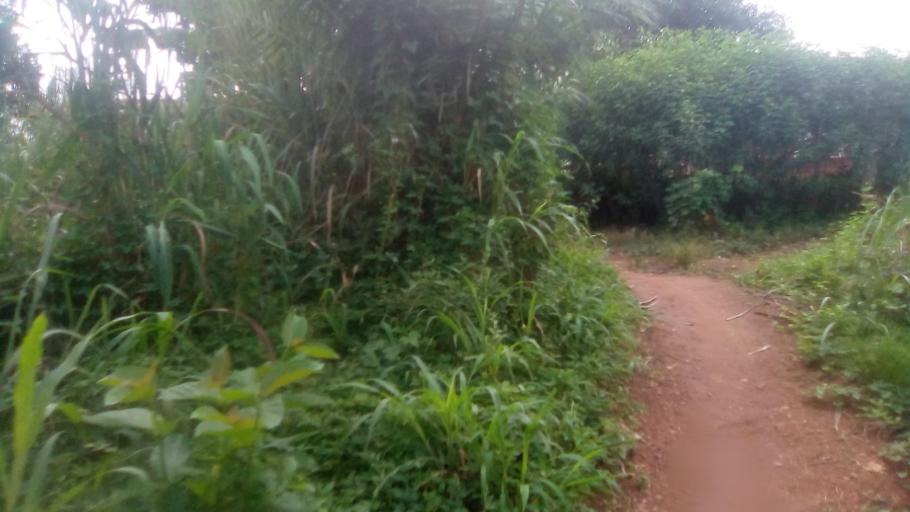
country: SL
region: Eastern Province
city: Kailahun
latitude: 8.2717
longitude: -10.5647
